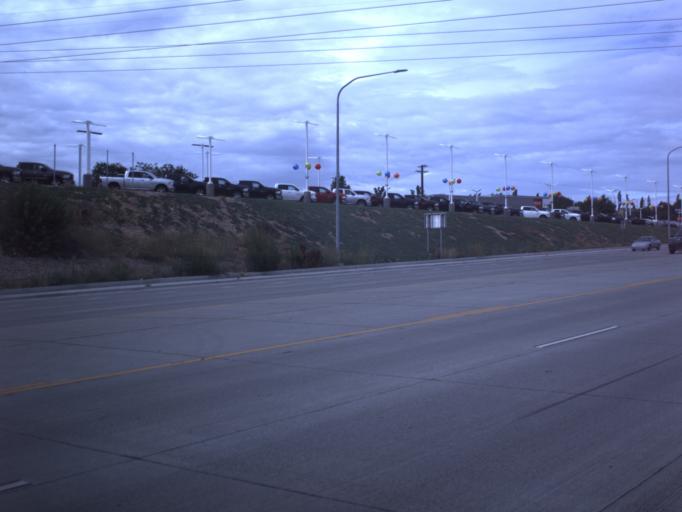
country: US
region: Utah
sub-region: Weber County
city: Riverdale
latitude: 41.1739
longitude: -112.0129
